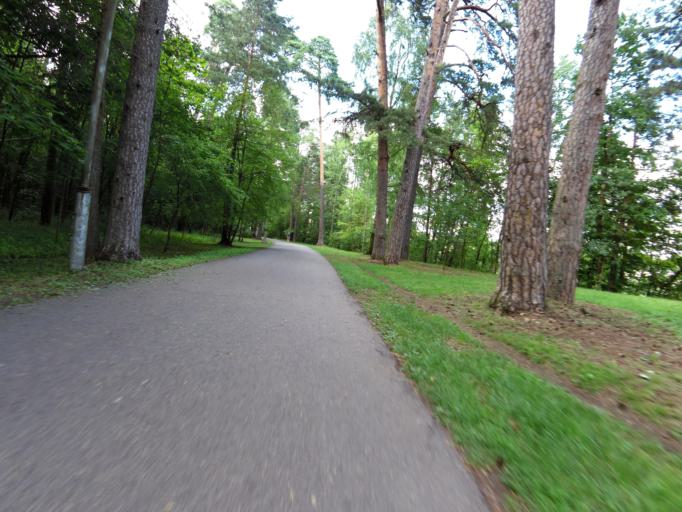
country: LT
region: Vilnius County
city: Vilkpede
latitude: 54.6881
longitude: 25.2431
